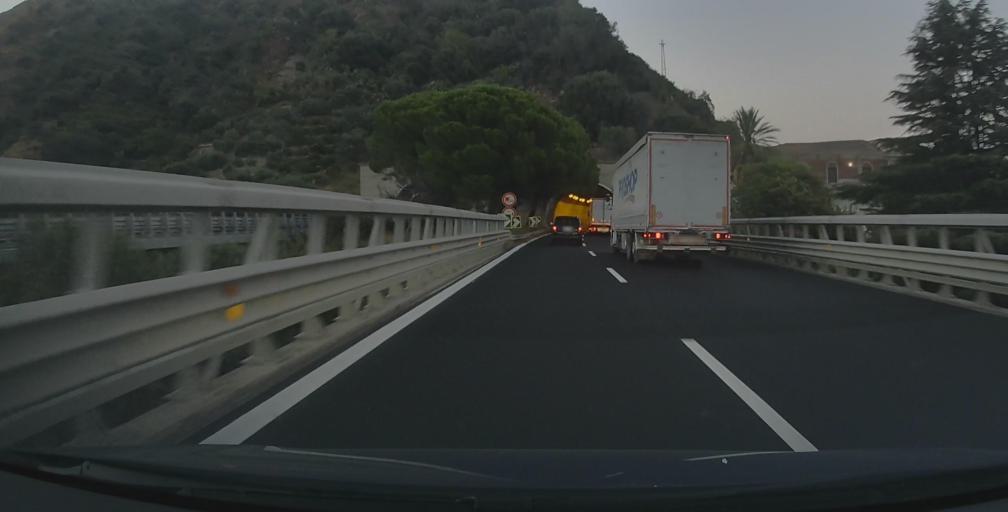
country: IT
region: Sicily
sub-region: Messina
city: Scaletta Zanclea
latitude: 38.0618
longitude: 15.4772
